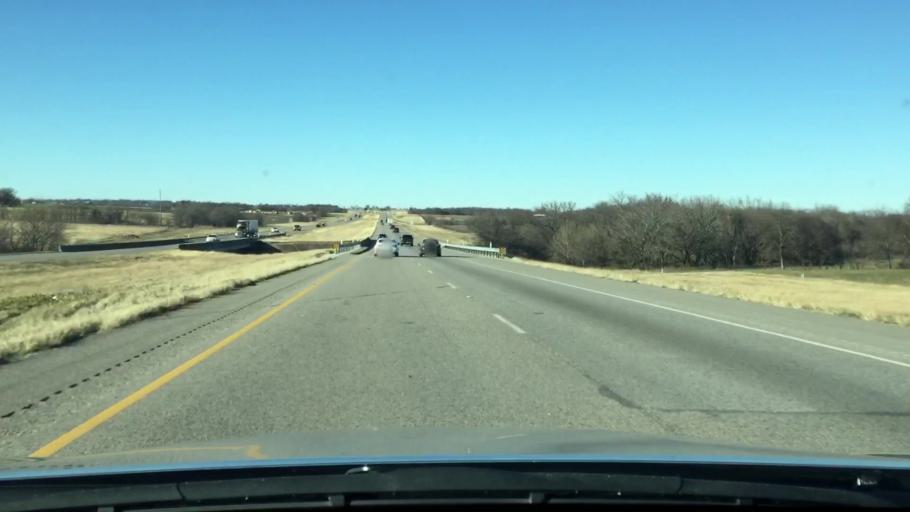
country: US
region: Texas
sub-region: Johnson County
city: Grandview
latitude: 32.2413
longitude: -97.1572
